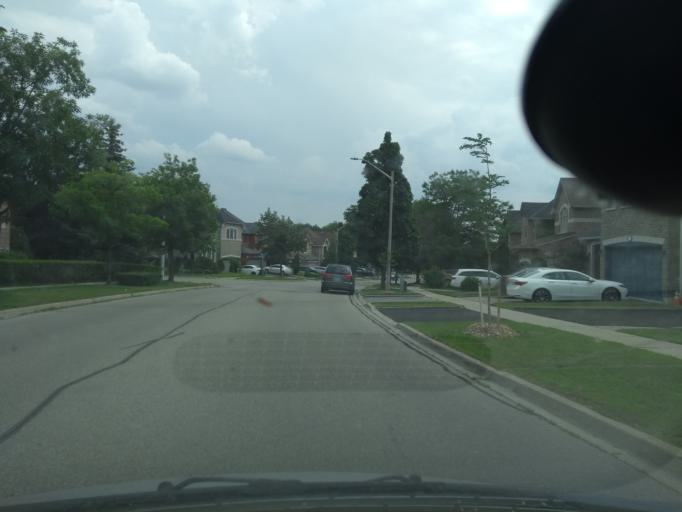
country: CA
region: Ontario
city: Mississauga
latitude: 43.6226
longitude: -79.6545
